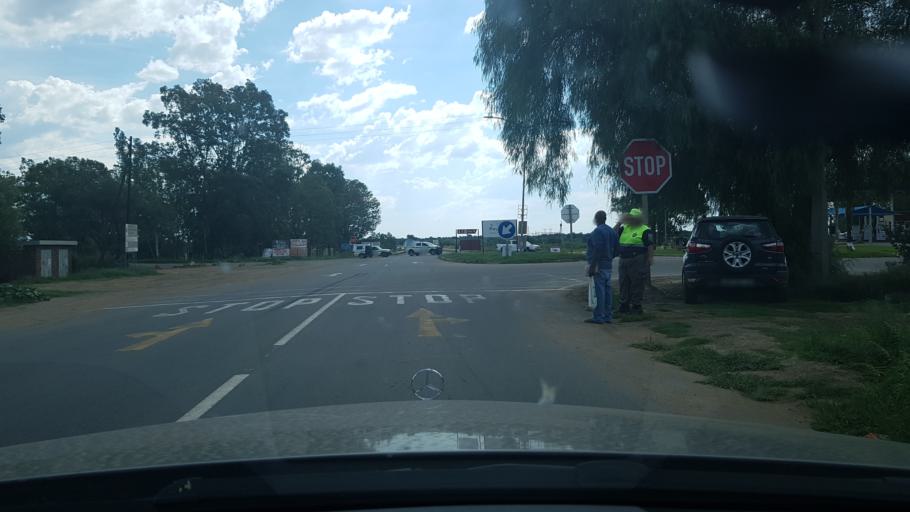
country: ZA
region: North-West
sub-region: Dr Ruth Segomotsi Mompati District Municipality
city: Bloemhof
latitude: -27.6525
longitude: 25.5969
